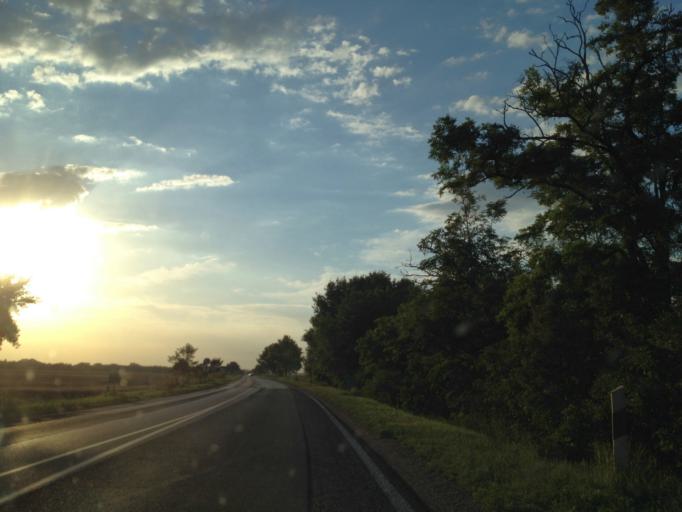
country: HU
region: Gyor-Moson-Sopron
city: Lebeny
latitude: 47.7847
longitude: 17.4107
